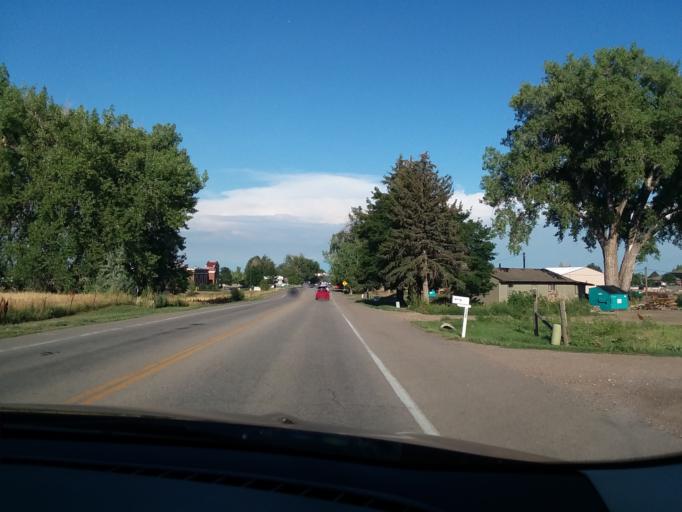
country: US
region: Colorado
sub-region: Larimer County
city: Fort Collins
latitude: 40.4947
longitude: -105.0810
